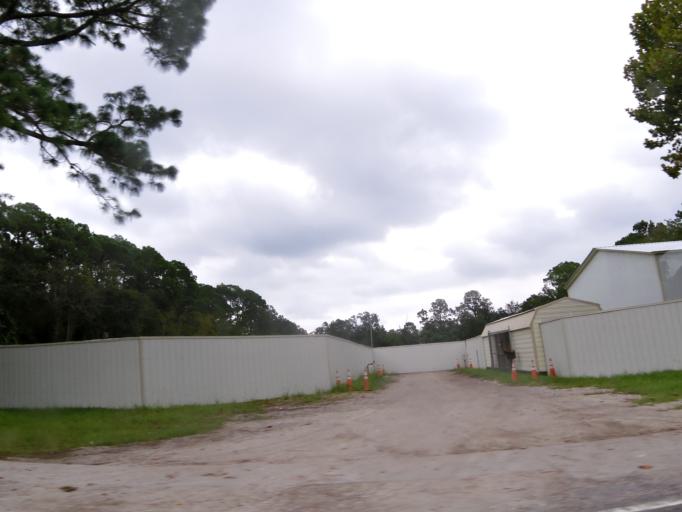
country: US
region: Florida
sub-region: Clay County
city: Bellair-Meadowbrook Terrace
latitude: 30.2622
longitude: -81.7733
